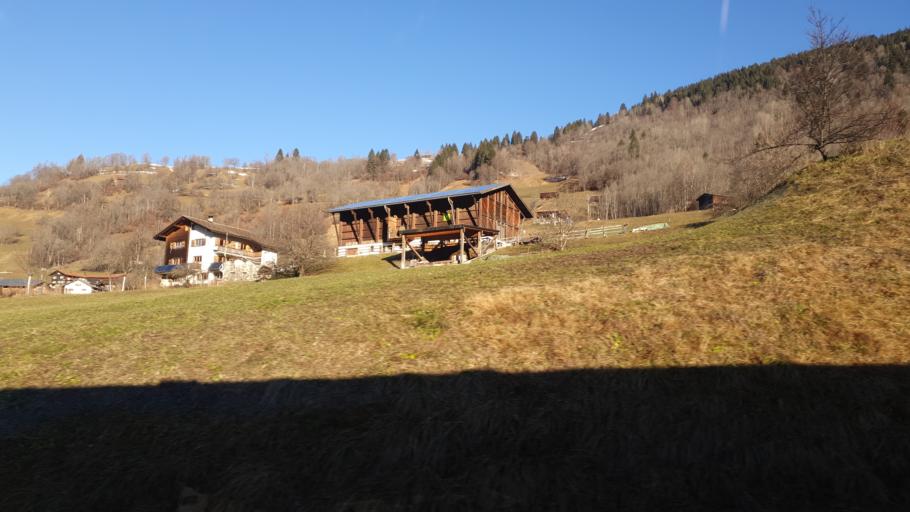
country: CH
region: Grisons
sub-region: Praettigau/Davos District
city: Luzein
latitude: 46.9120
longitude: 9.7952
